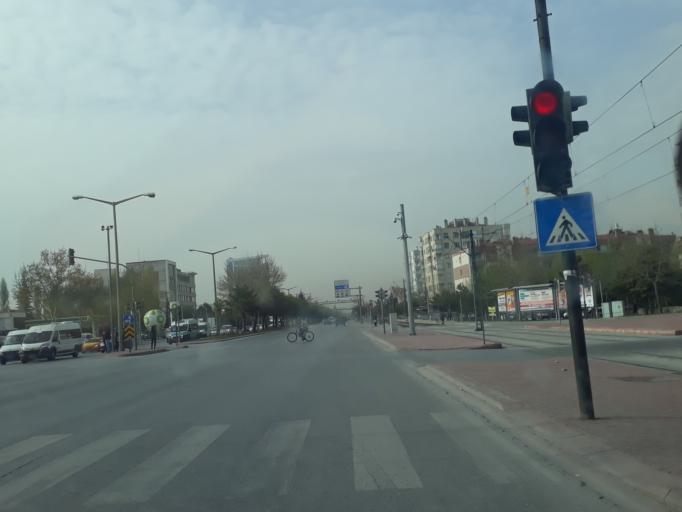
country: TR
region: Konya
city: Selcuklu
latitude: 37.9419
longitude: 32.5117
